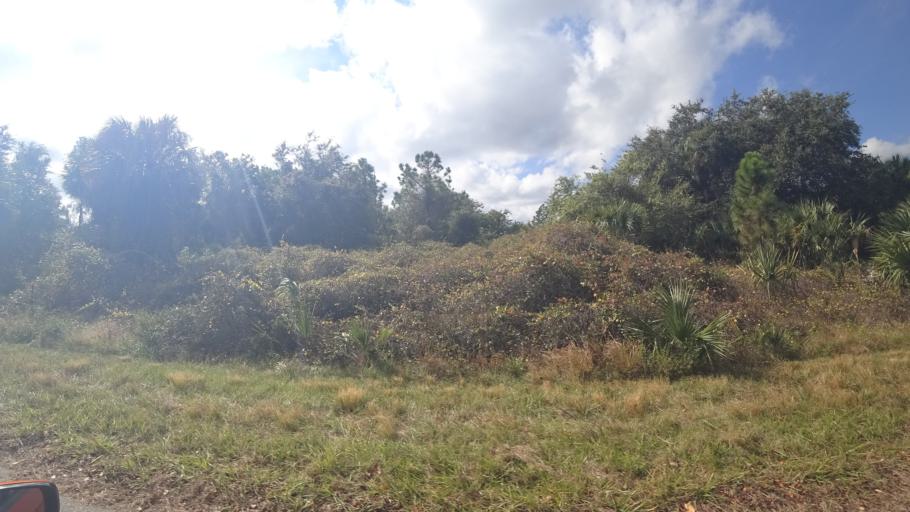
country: US
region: Florida
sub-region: Charlotte County
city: Port Charlotte
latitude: 27.0465
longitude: -82.1326
